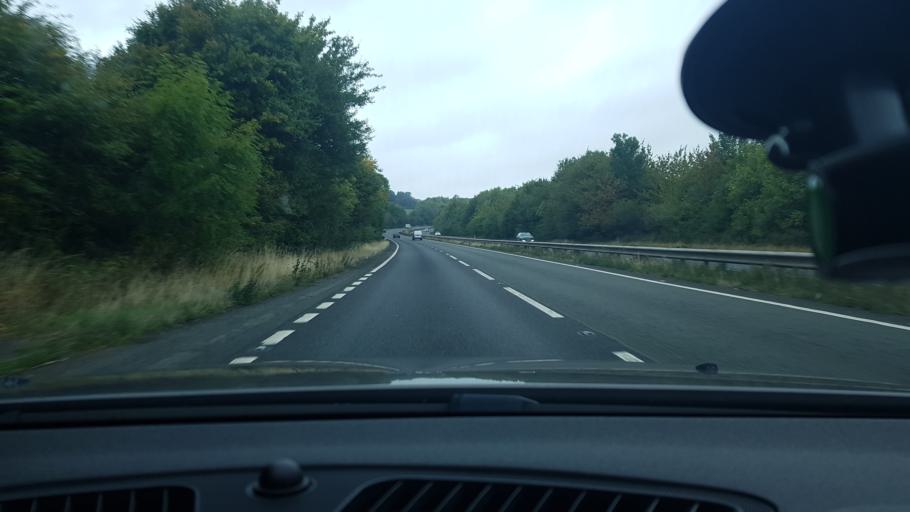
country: GB
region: England
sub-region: Hampshire
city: Highclere
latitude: 51.3224
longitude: -1.3416
